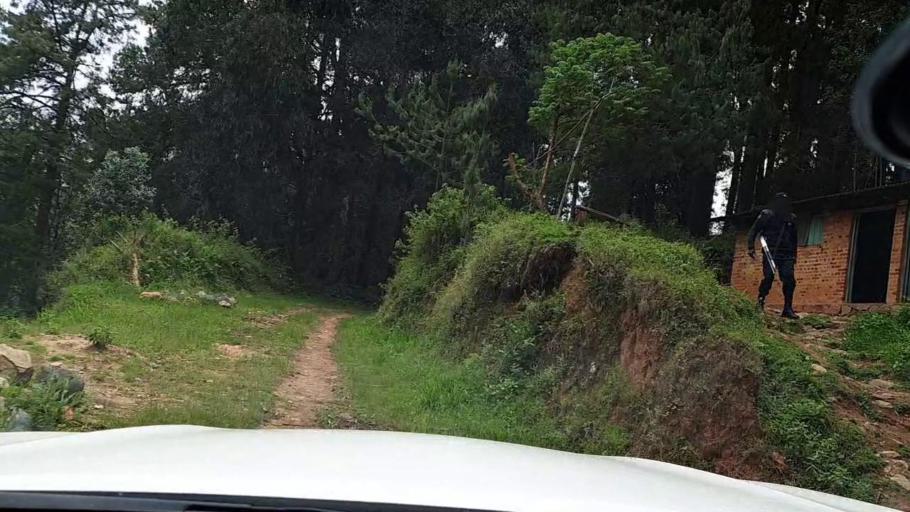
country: RW
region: Western Province
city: Kibuye
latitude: -2.2856
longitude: 29.3037
